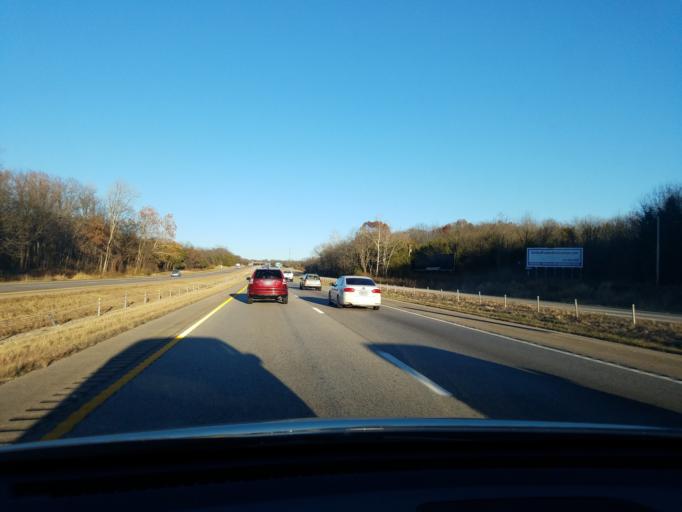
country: US
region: Missouri
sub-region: Franklin County
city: Villa Ridge
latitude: 38.4581
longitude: -90.8719
